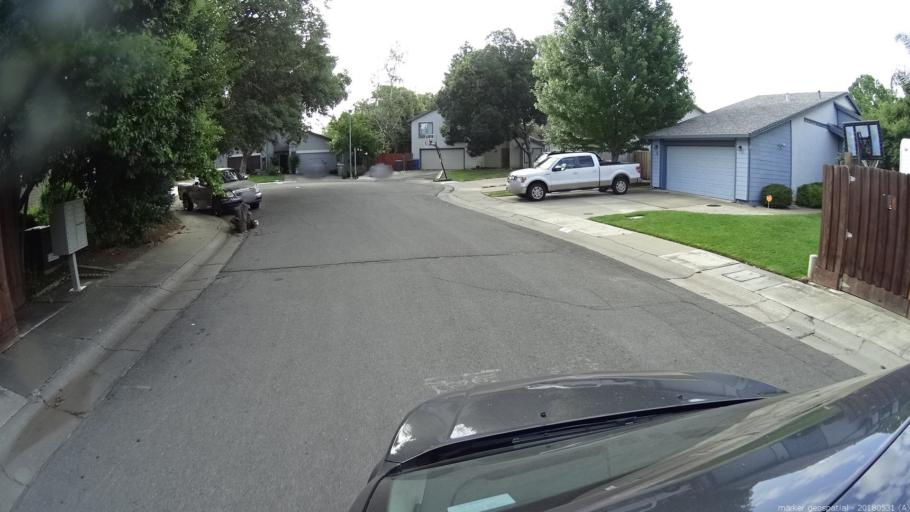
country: US
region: California
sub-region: Sacramento County
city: Sacramento
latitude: 38.6222
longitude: -121.4894
